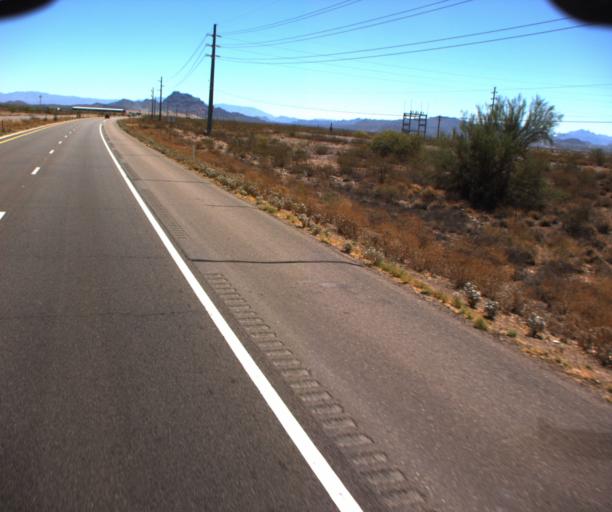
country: US
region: Arizona
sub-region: Maricopa County
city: Mesa
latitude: 33.5004
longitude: -111.7977
